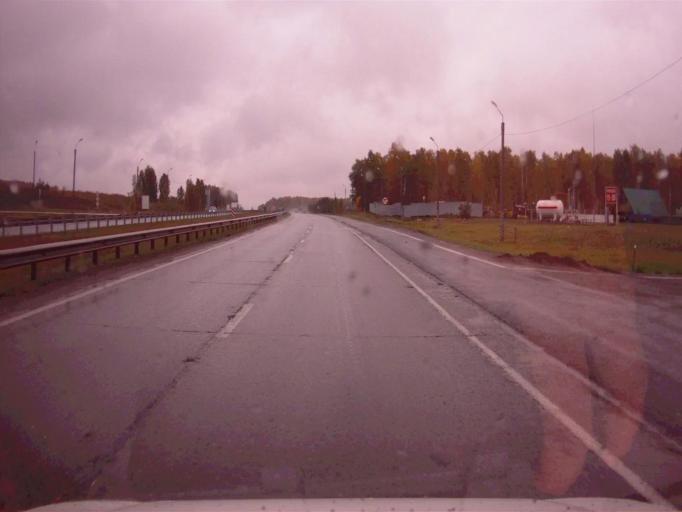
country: RU
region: Chelyabinsk
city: Dolgoderevenskoye
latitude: 55.3260
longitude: 61.3286
